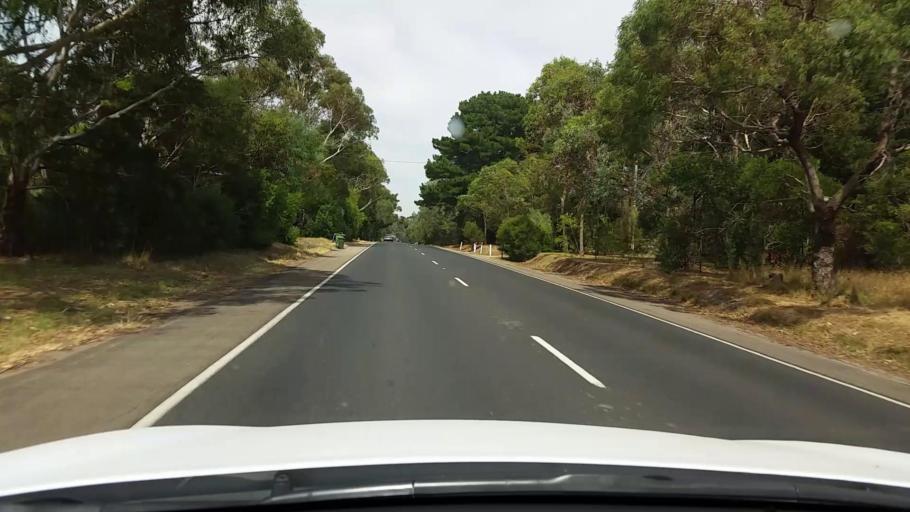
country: AU
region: Victoria
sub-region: Mornington Peninsula
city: Balnarring
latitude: -38.3484
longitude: 145.1629
